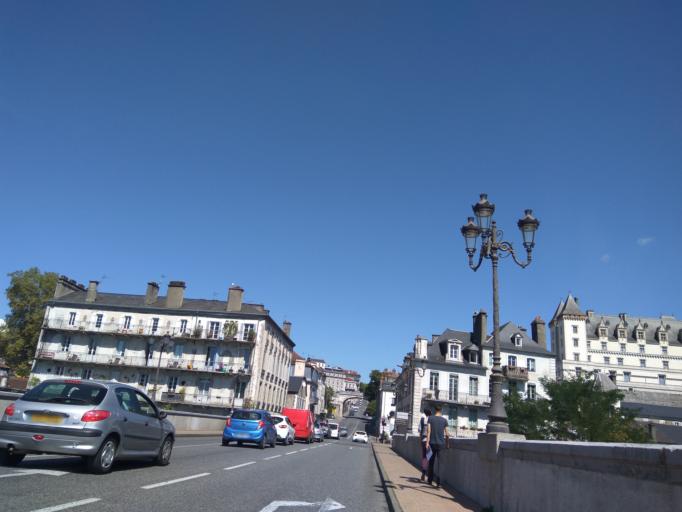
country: FR
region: Aquitaine
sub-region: Departement des Pyrenees-Atlantiques
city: Jurancon
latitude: 43.2934
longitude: -0.3776
